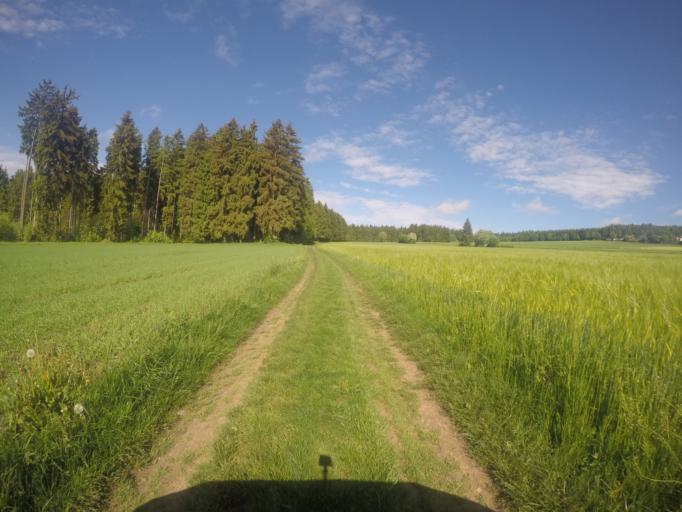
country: DE
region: Bavaria
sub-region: Upper Franconia
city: Schonwald
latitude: 50.1940
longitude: 12.0764
